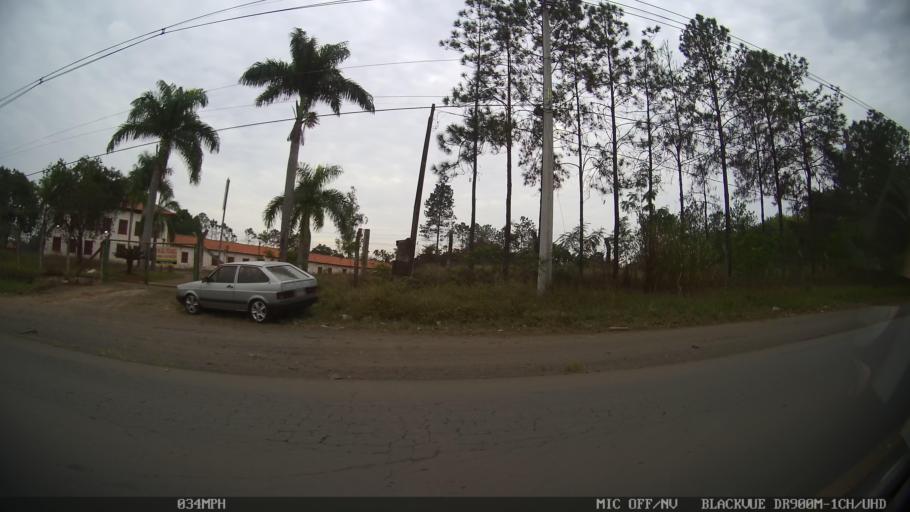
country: BR
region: Sao Paulo
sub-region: Americana
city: Americana
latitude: -22.6953
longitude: -47.2881
